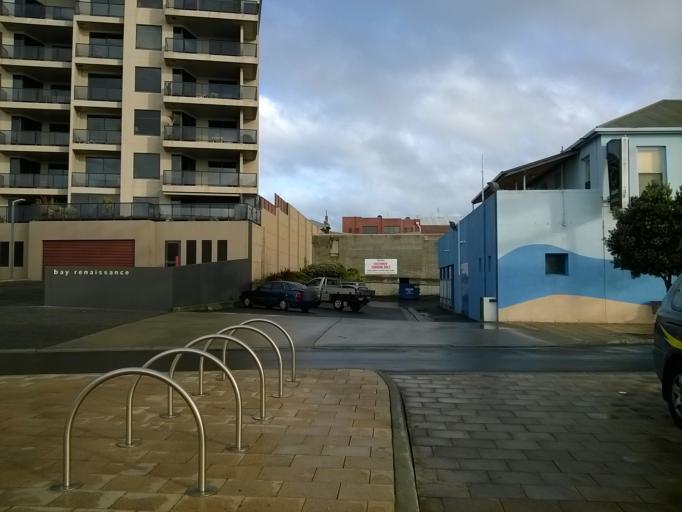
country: AU
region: Tasmania
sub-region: Burnie
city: Burnie
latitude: -41.0499
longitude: 145.9075
